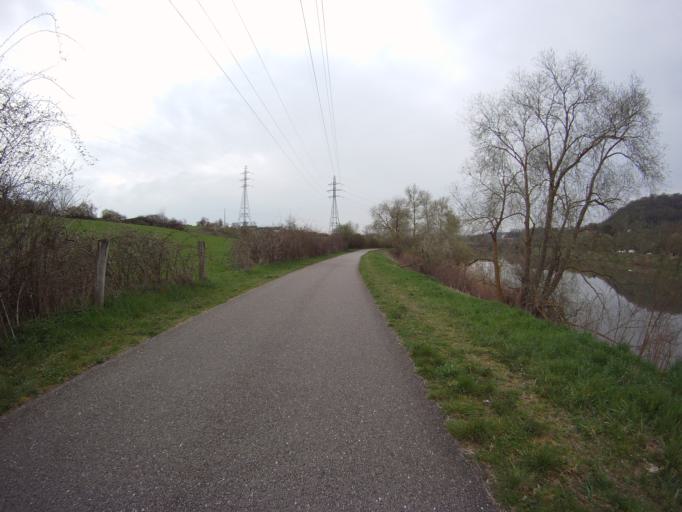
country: FR
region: Lorraine
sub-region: Departement de Meurthe-et-Moselle
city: Champigneulles
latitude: 48.7283
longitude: 6.1766
